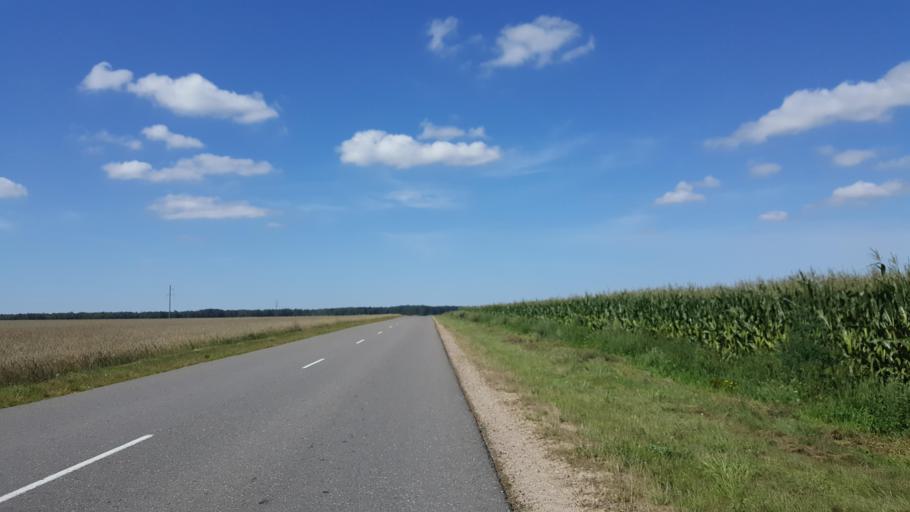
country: BY
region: Brest
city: Kamyanyets
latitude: 52.3866
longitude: 23.7234
